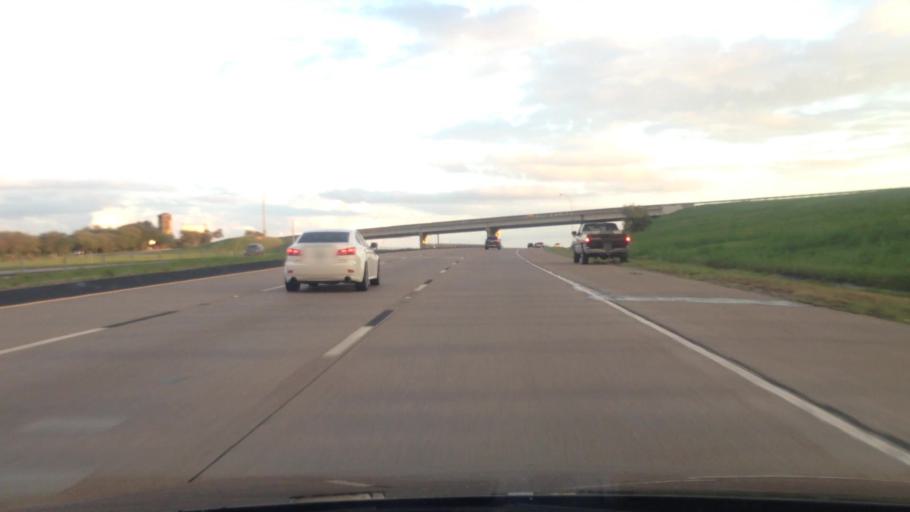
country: US
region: Texas
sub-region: Tarrant County
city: Benbrook
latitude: 32.7045
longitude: -97.4740
